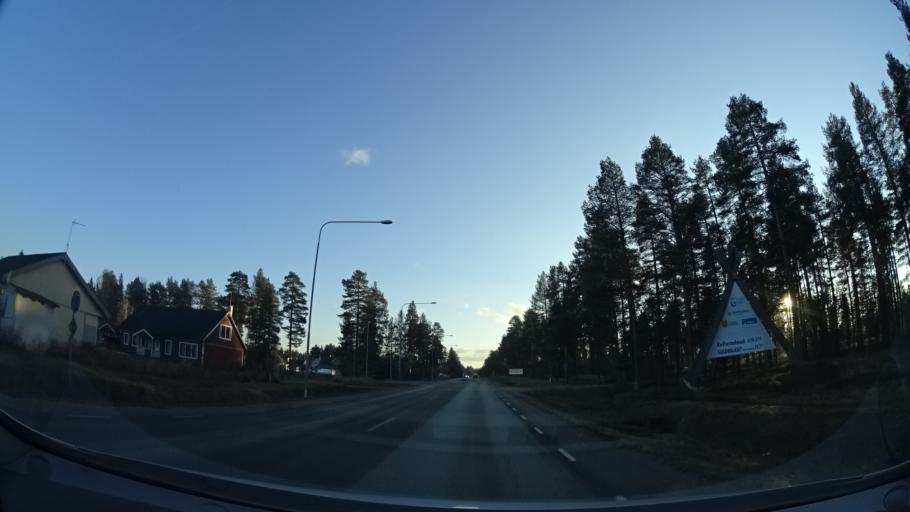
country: SE
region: Vaesterbotten
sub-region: Lycksele Kommun
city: Lycksele
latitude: 64.6010
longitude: 18.7008
